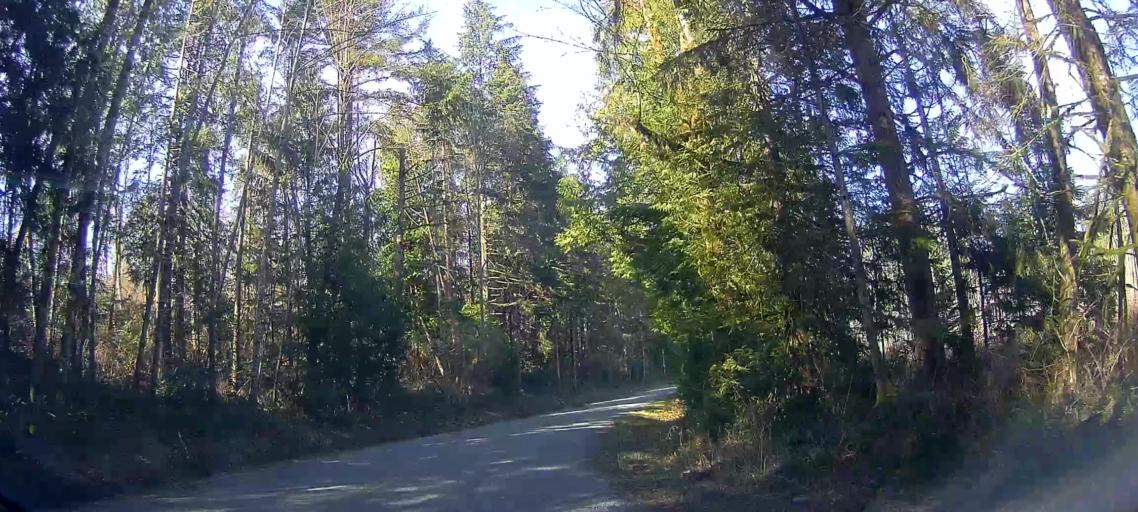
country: US
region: Washington
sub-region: Whatcom County
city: Sudden Valley
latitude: 48.6095
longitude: -122.3667
